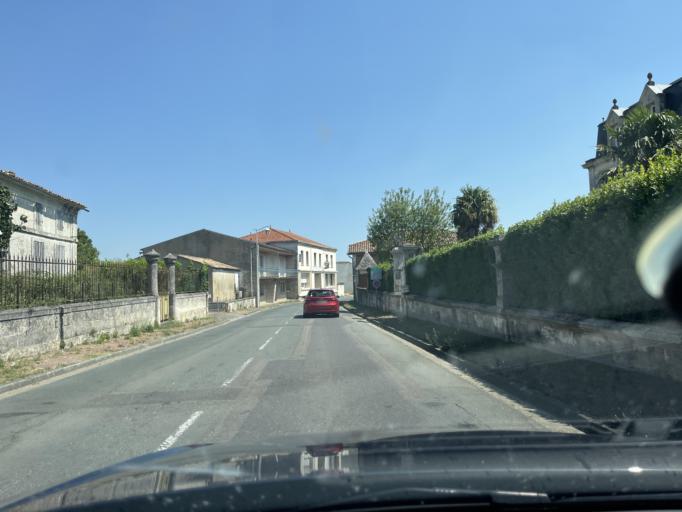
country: FR
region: Poitou-Charentes
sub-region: Departement de la Charente-Maritime
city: Mortagne-sur-Gironde
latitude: 45.4581
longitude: -0.6920
